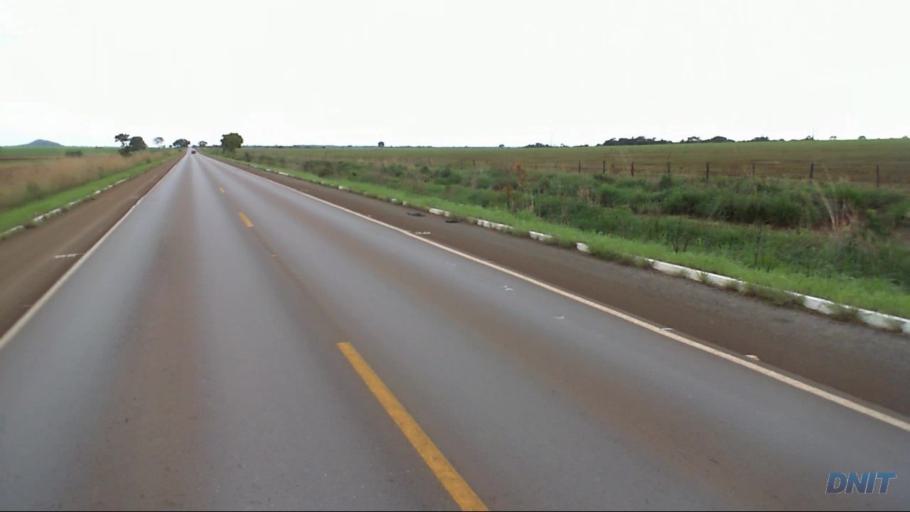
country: BR
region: Goias
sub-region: Barro Alto
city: Barro Alto
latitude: -14.8221
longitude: -49.0387
